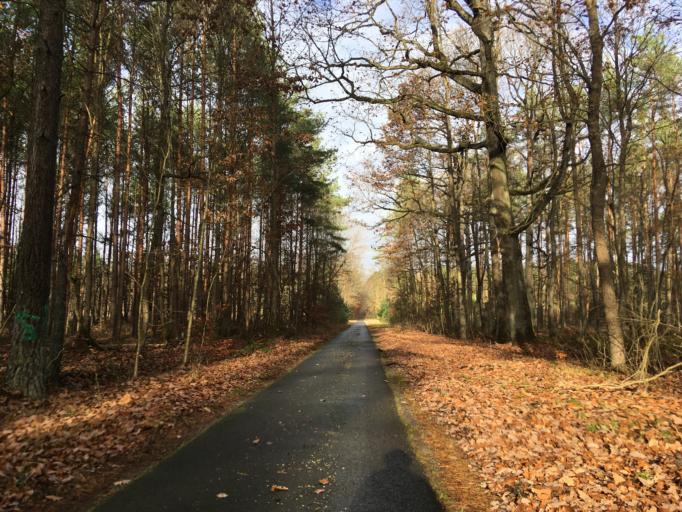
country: DE
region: Brandenburg
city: Tauer
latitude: 51.9284
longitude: 14.5115
